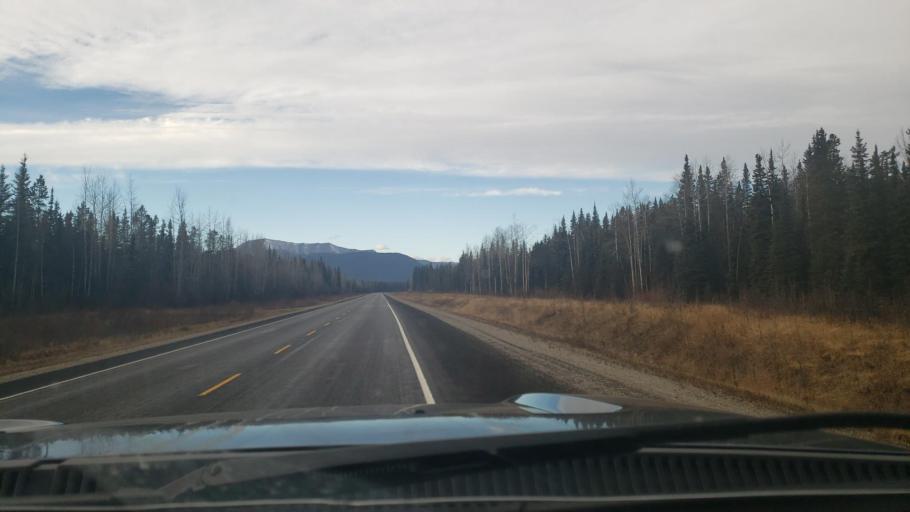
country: CA
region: British Columbia
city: Fort Nelson
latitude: 58.6588
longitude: -124.1222
